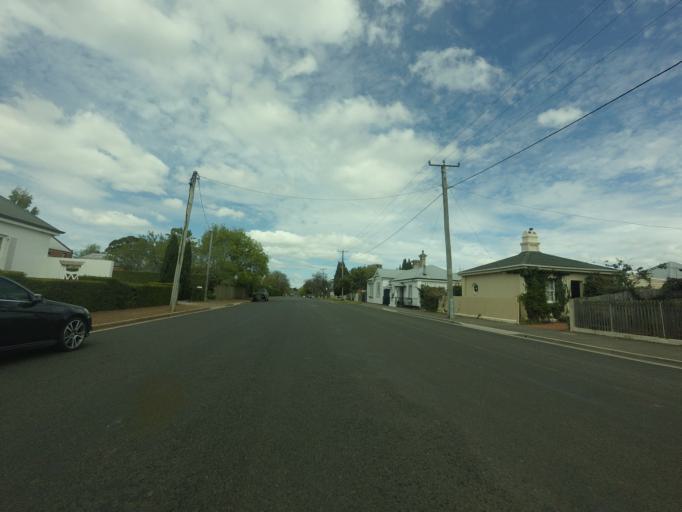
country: AU
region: Tasmania
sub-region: Northern Midlands
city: Longford
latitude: -41.5971
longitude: 147.1231
